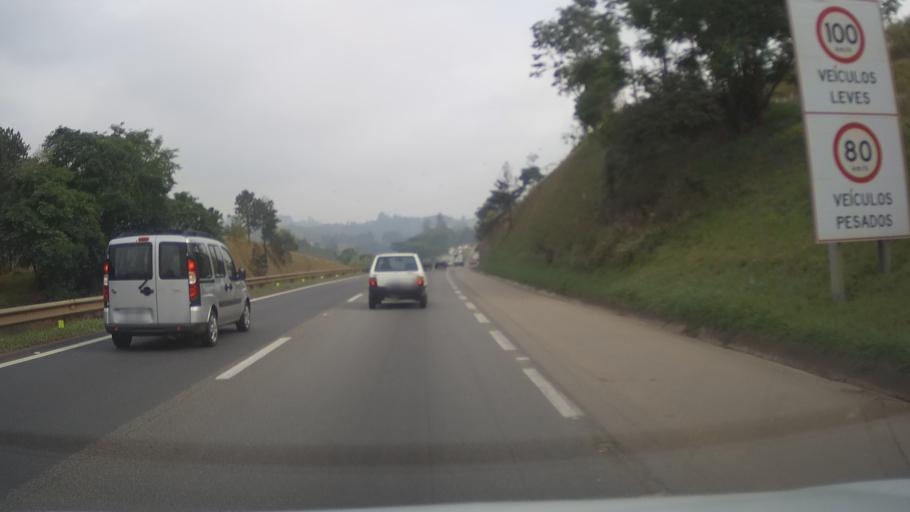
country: BR
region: Sao Paulo
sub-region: Atibaia
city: Atibaia
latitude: -23.0662
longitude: -46.5698
